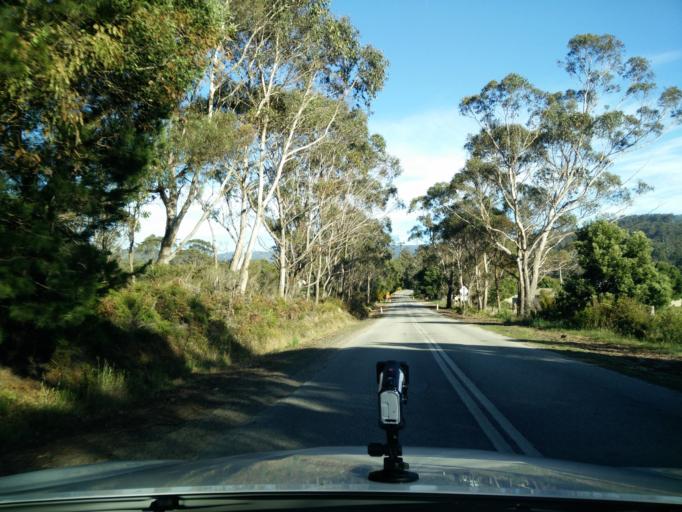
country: AU
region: Tasmania
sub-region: Break O'Day
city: St Helens
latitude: -41.2607
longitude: 148.0879
